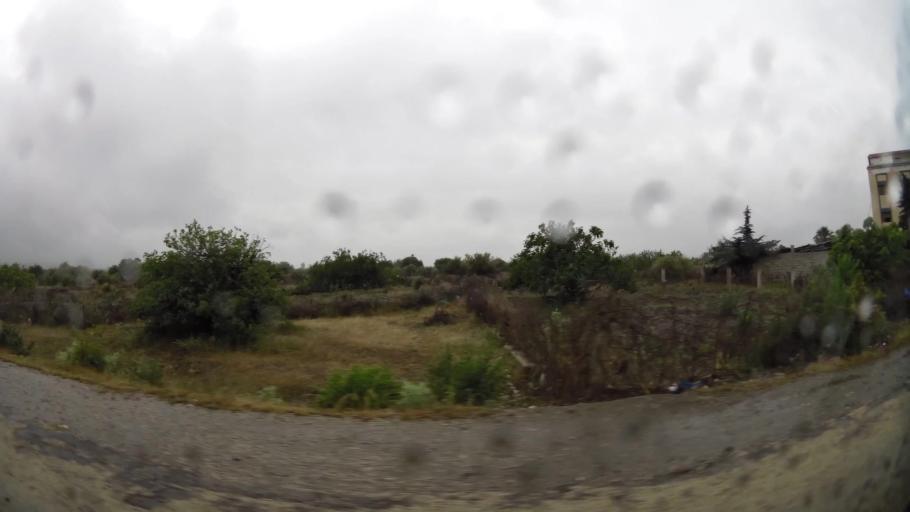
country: MA
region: Taza-Al Hoceima-Taounate
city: Imzourene
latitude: 35.1382
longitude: -3.7845
